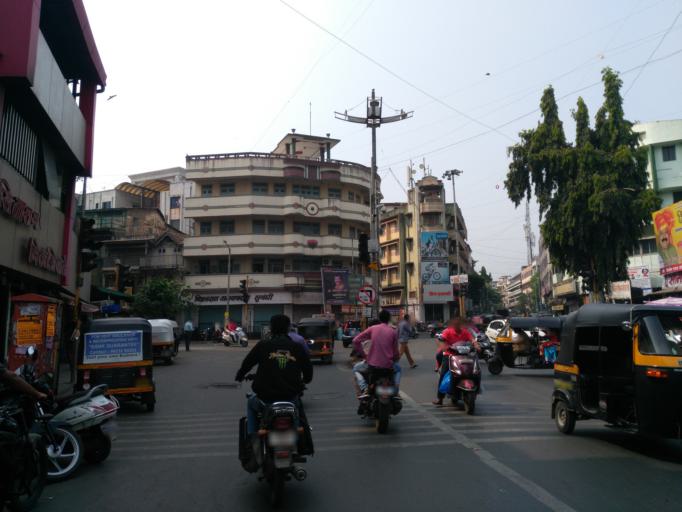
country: IN
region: Maharashtra
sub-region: Pune Division
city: Pune
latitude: 18.5187
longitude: 73.8599
